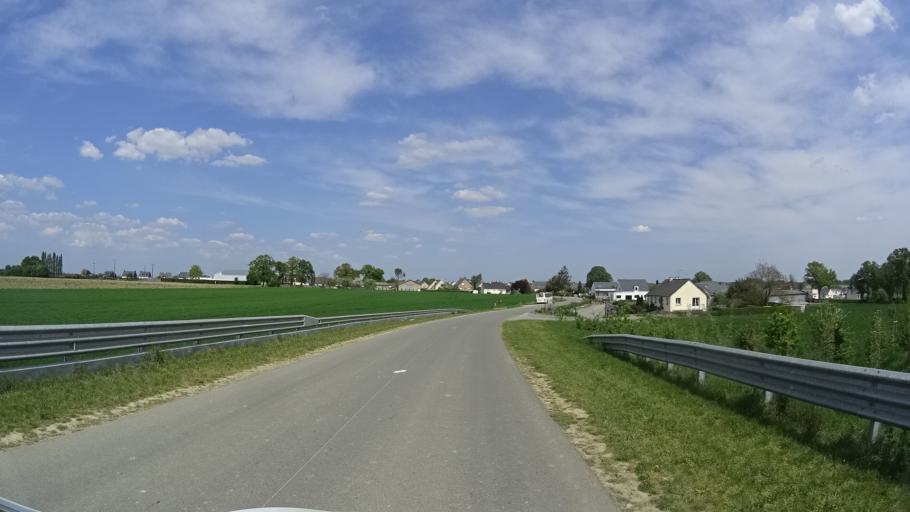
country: FR
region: Brittany
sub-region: Departement d'Ille-et-Vilaine
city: Torce
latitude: 48.0578
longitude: -1.2694
